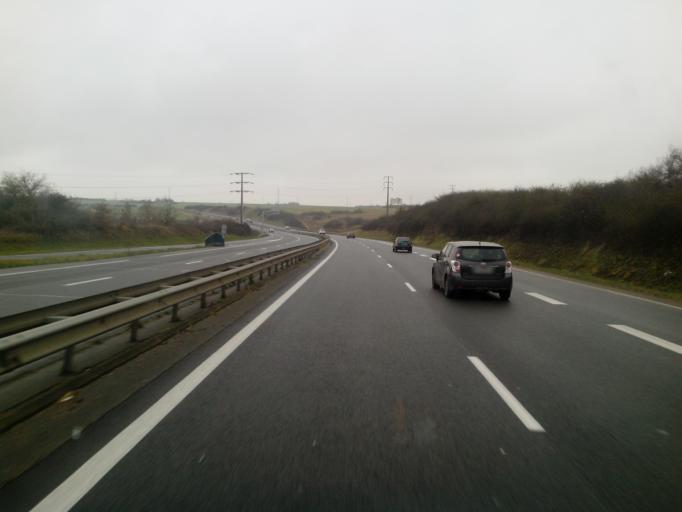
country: FR
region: Poitou-Charentes
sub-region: Departement de la Vienne
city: Montamise
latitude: 46.6119
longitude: 0.3882
